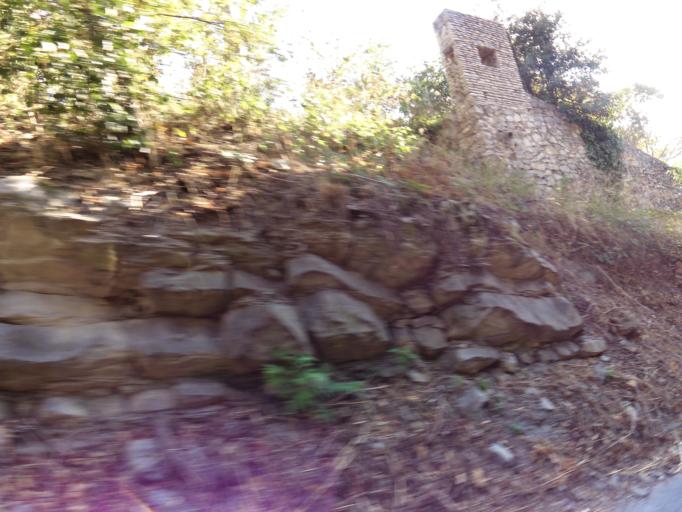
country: FR
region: Languedoc-Roussillon
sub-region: Departement du Gard
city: Nimes
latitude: 43.8474
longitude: 4.3473
